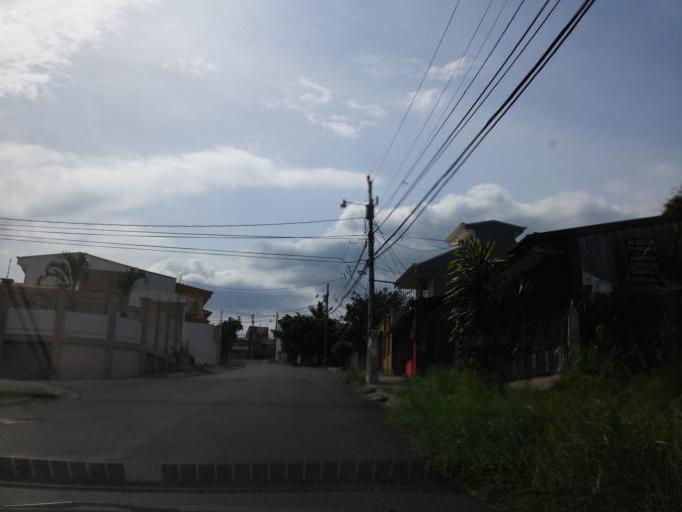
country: CR
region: Alajuela
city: Alajuela
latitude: 10.0137
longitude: -84.1985
